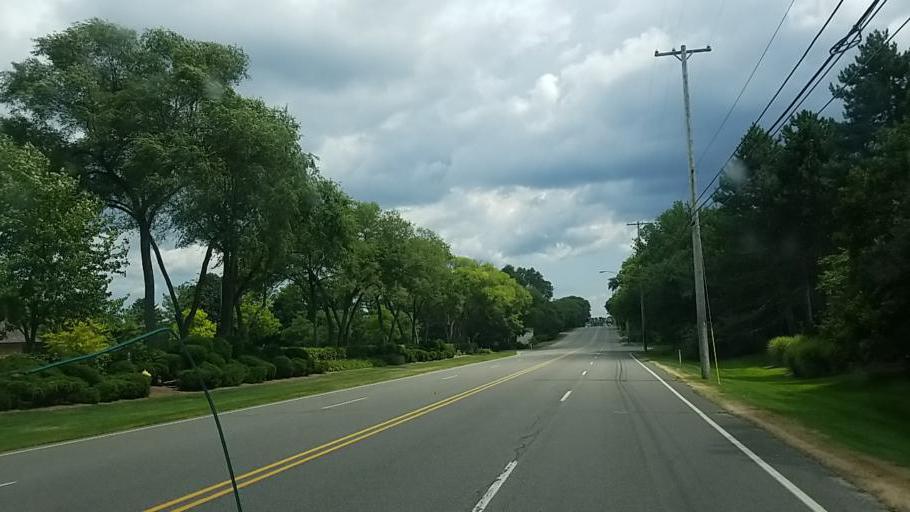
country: US
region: Michigan
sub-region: Kent County
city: East Grand Rapids
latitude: 42.9517
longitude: -85.5776
